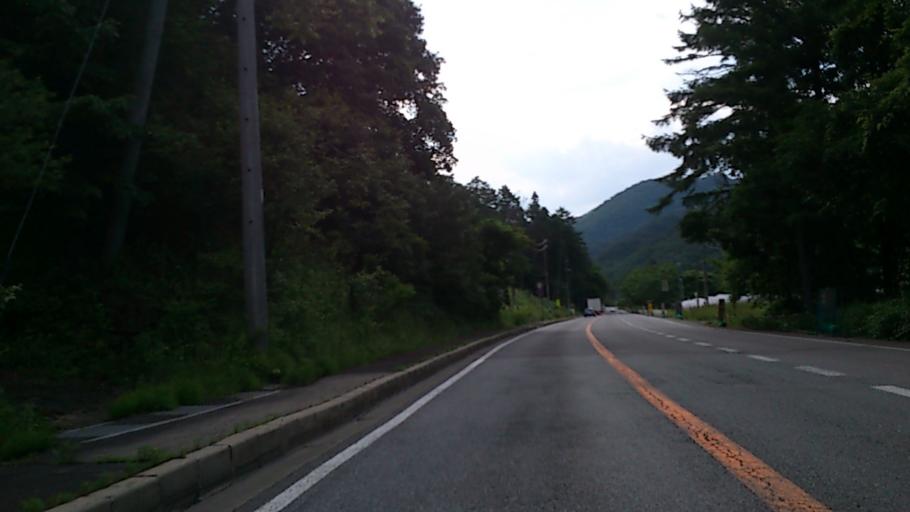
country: JP
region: Nagano
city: Saku
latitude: 36.2140
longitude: 138.5973
